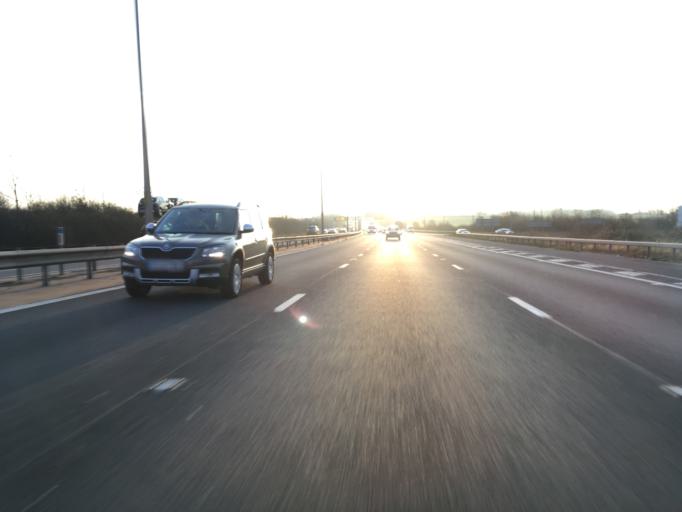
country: GB
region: England
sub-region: Worcestershire
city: Bredon
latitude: 52.0651
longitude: -2.1545
